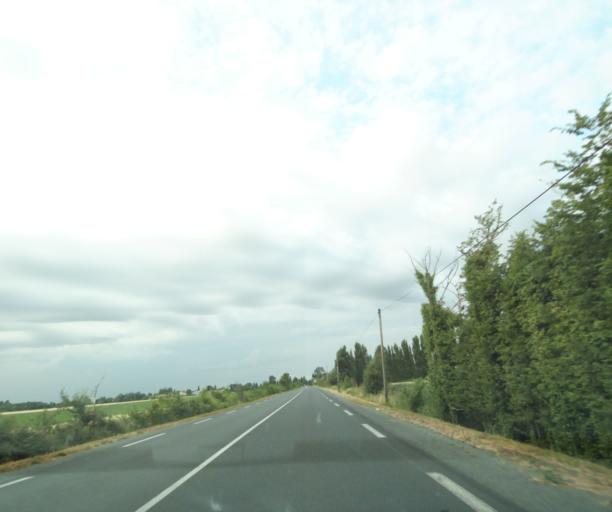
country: FR
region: Pays de la Loire
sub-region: Departement de la Vendee
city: Chaille-les-Marais
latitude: 46.3594
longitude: -0.9908
